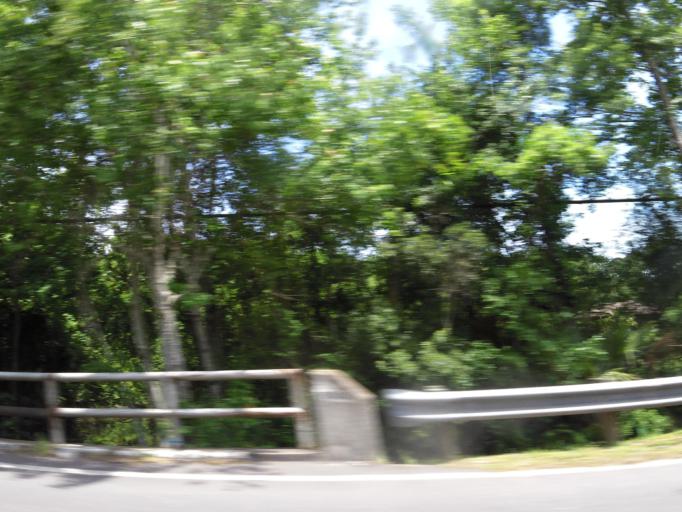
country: US
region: Florida
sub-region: Duval County
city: Jacksonville
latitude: 30.4593
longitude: -81.5337
